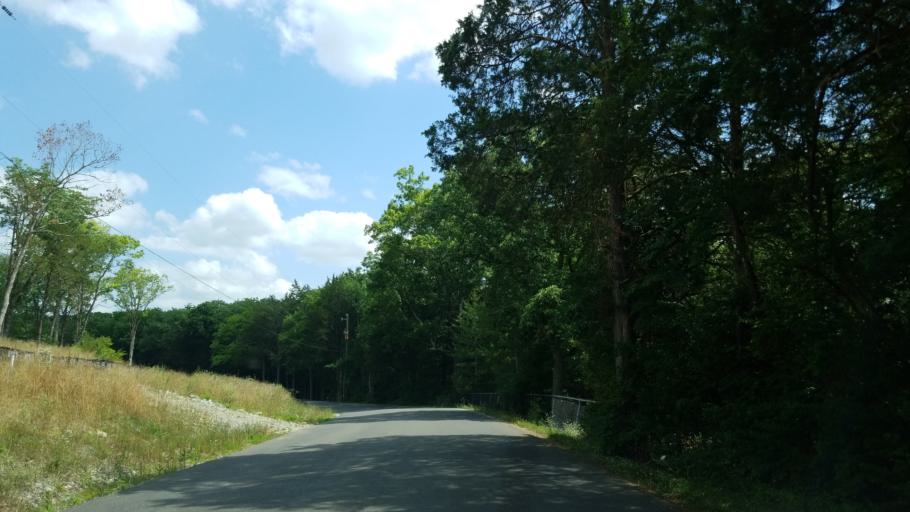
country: US
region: Tennessee
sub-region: Davidson County
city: Forest Hills
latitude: 36.0383
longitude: -86.8690
